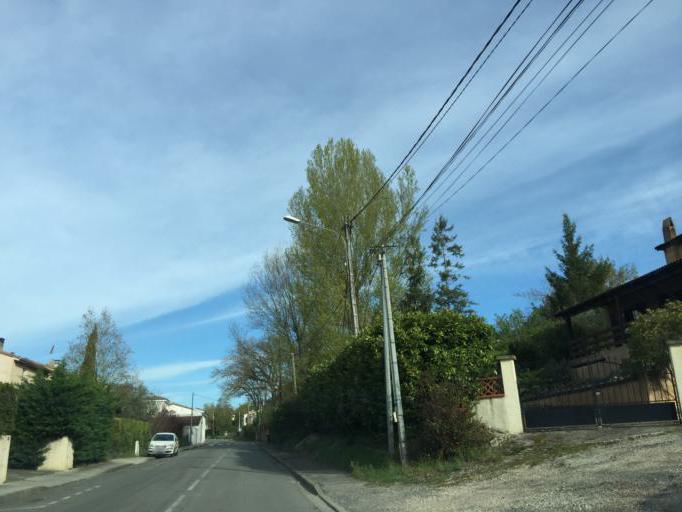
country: FR
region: Midi-Pyrenees
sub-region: Departement de la Haute-Garonne
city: Montastruc-la-Conseillere
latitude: 43.7176
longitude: 1.5976
